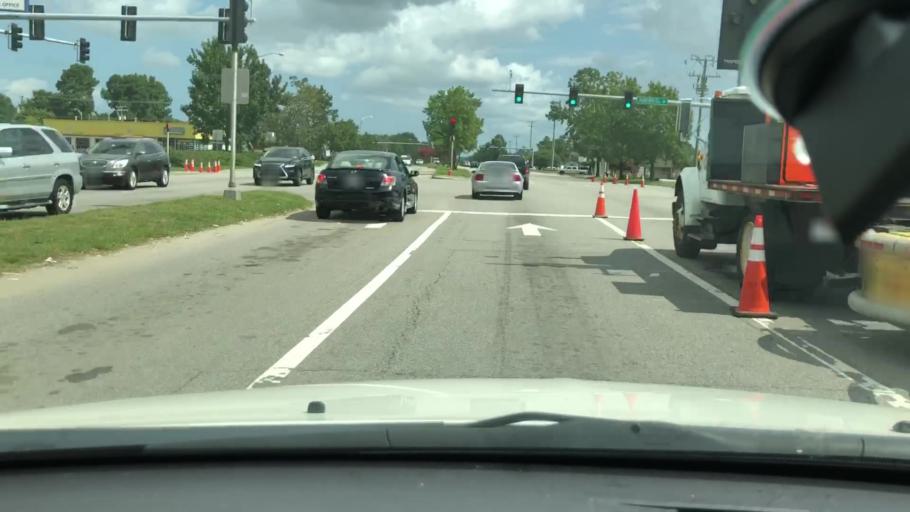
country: US
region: Virginia
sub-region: City of Chesapeake
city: Chesapeake
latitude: 36.8091
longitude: -76.2192
